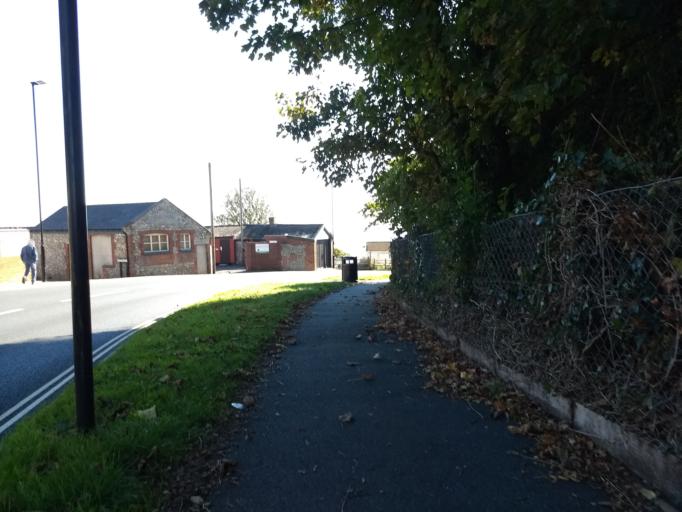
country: GB
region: England
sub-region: Isle of Wight
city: Ventnor
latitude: 50.5969
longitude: -1.2149
